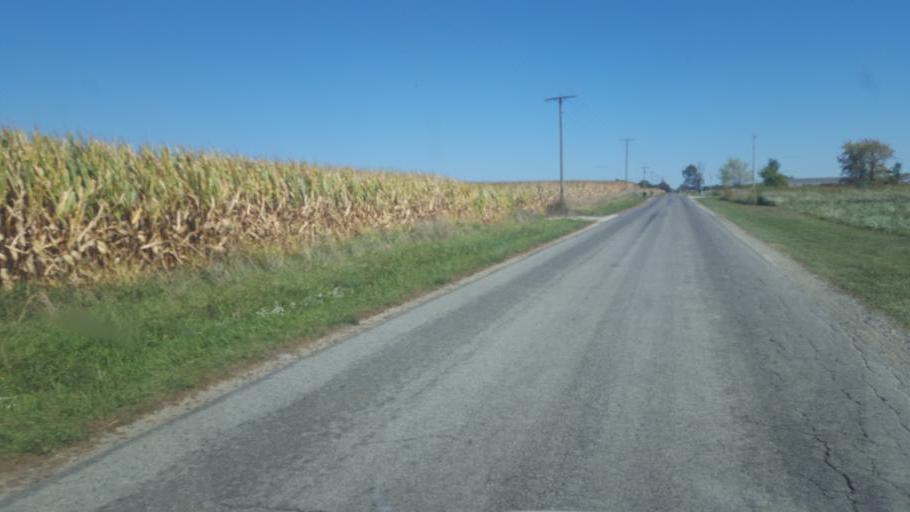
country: US
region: Ohio
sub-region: Huron County
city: Greenwich
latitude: 40.9932
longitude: -82.5153
